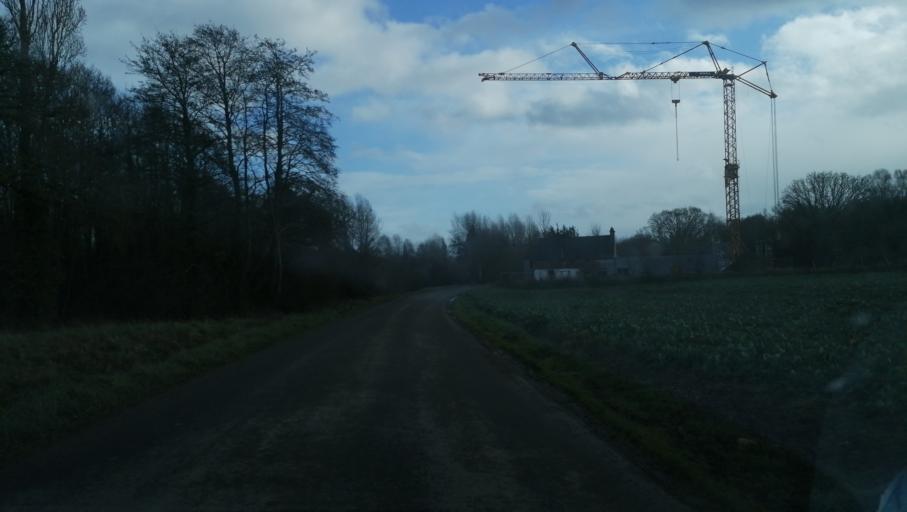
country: FR
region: Brittany
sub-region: Departement des Cotes-d'Armor
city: Lantic
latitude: 48.5917
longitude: -2.9180
